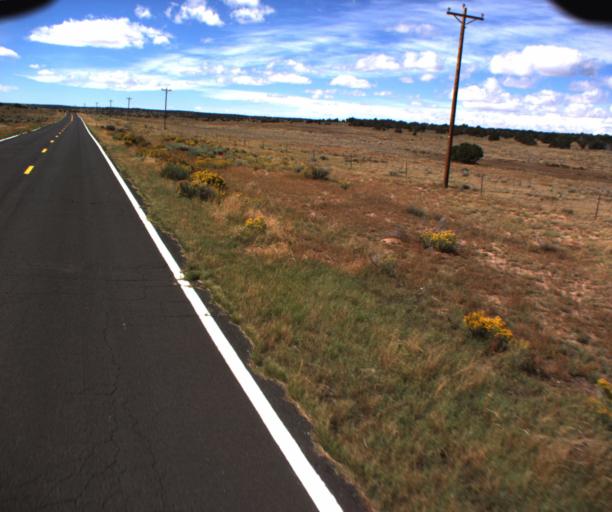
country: US
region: New Mexico
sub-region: McKinley County
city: Zuni Pueblo
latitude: 35.0117
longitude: -109.0662
